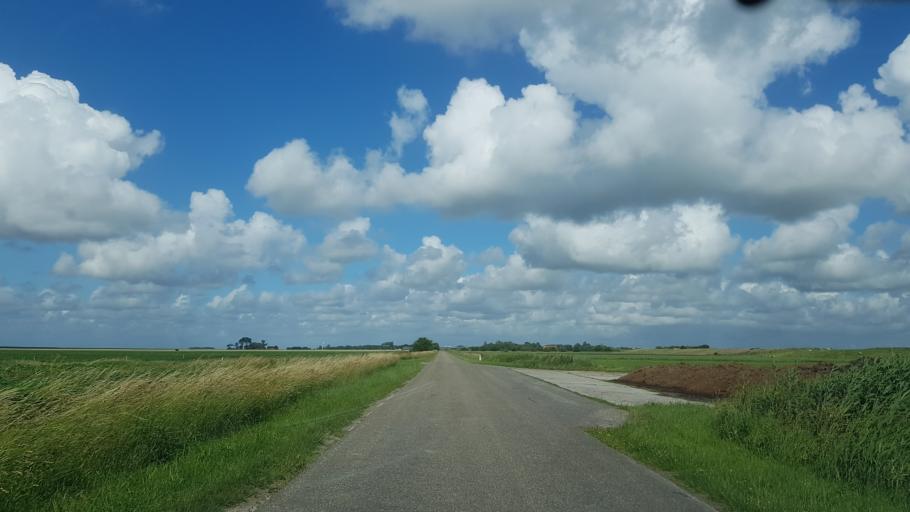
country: NL
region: Groningen
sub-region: Gemeente Winsum
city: Winsum
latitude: 53.4120
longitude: 6.5794
